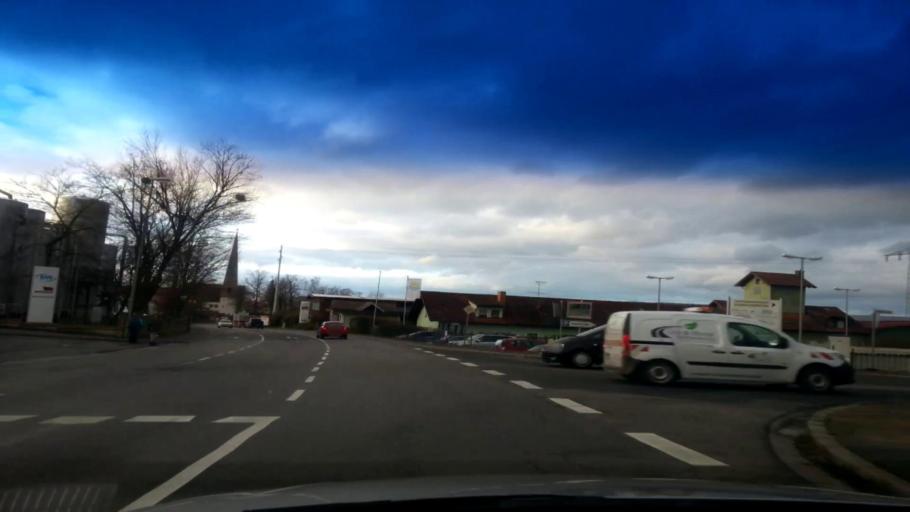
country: DE
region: Bavaria
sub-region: Upper Franconia
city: Zapfendorf
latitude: 50.0151
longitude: 10.9388
